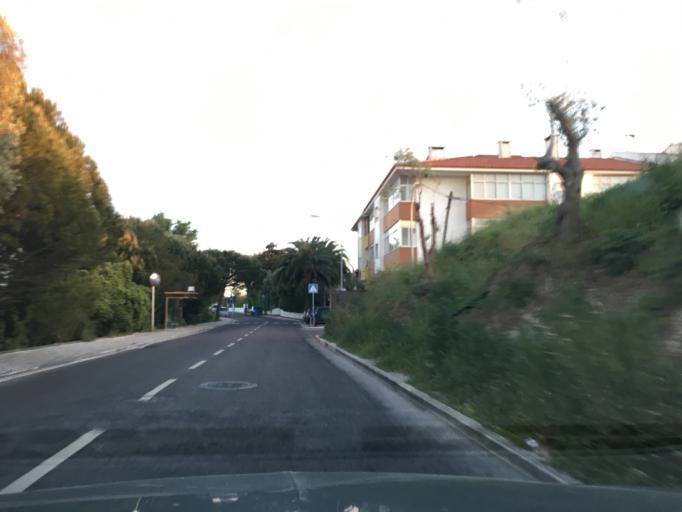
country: PT
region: Lisbon
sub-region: Oeiras
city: Terrugem
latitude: 38.7054
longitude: -9.2880
